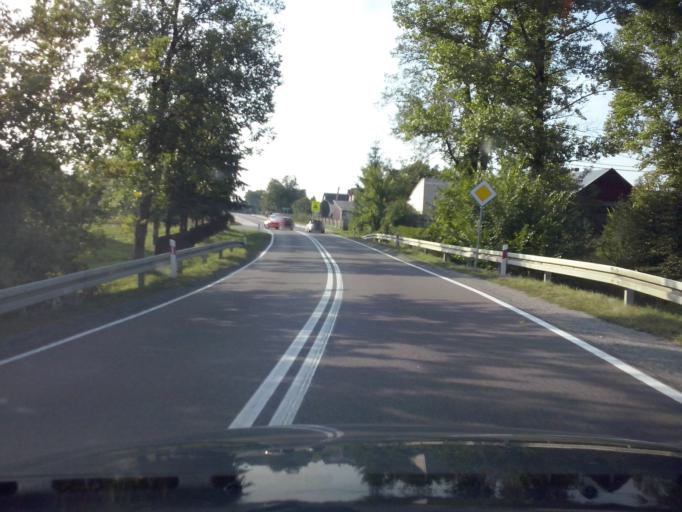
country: PL
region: Subcarpathian Voivodeship
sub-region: Powiat nizanski
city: Krzeszow
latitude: 50.3679
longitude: 22.3202
